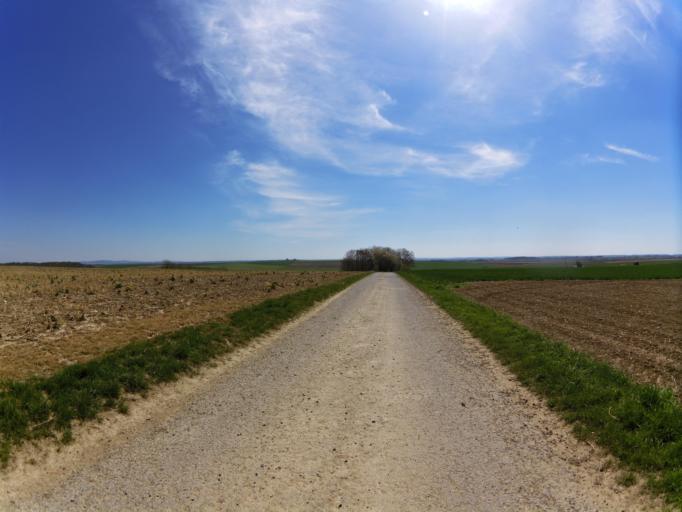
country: DE
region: Bavaria
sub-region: Regierungsbezirk Unterfranken
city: Eibelstadt
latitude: 49.6961
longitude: 9.9865
